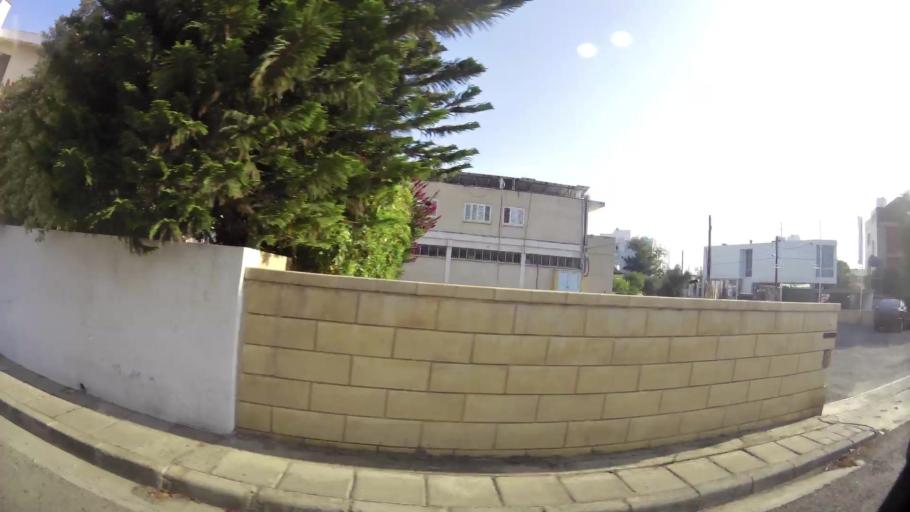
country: CY
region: Lefkosia
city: Nicosia
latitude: 35.1740
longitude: 33.3286
